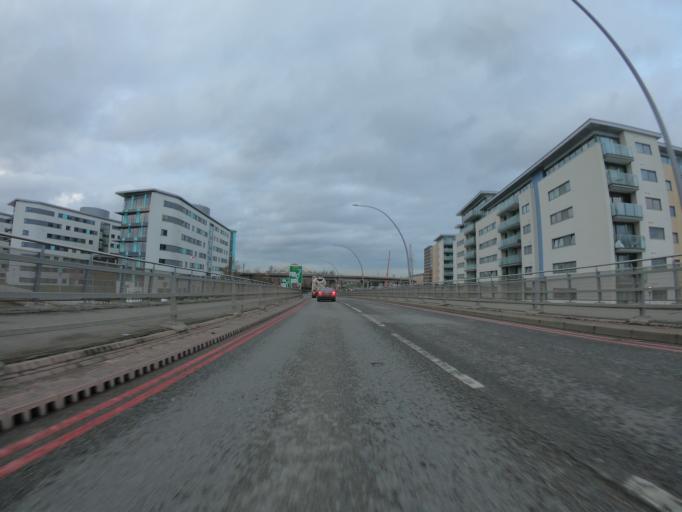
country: GB
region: England
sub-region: Greater London
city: Woolwich
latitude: 51.5062
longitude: 0.0713
